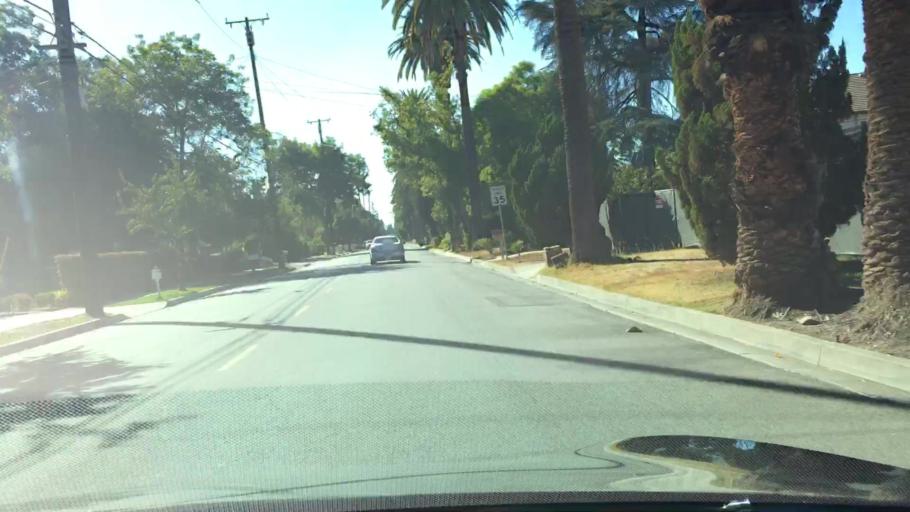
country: US
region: California
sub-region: Los Angeles County
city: North El Monte
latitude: 34.1143
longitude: -118.0250
